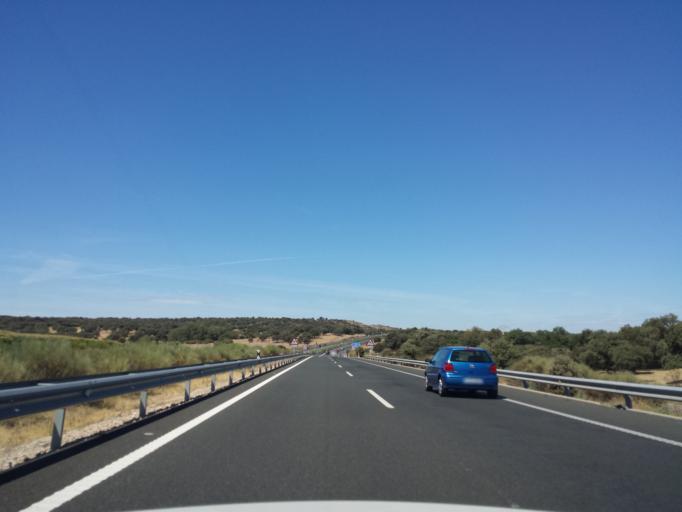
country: ES
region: Extremadura
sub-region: Provincia de Caceres
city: Peraleda de la Mata
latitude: 39.8887
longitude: -5.4865
